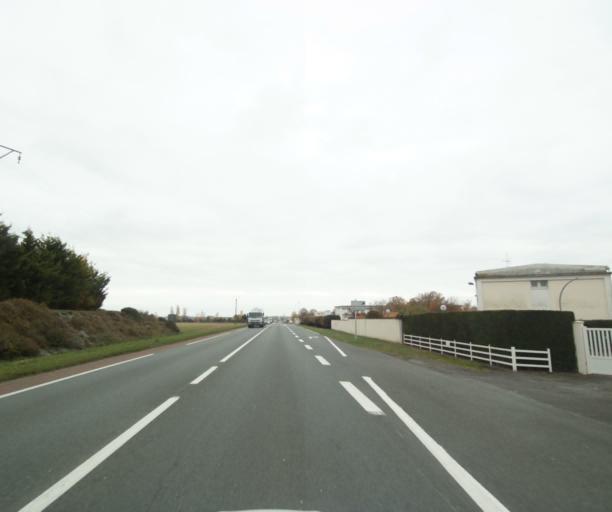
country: FR
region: Poitou-Charentes
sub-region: Departement de la Charente-Maritime
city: Les Gonds
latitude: 45.7116
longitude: -0.6309
